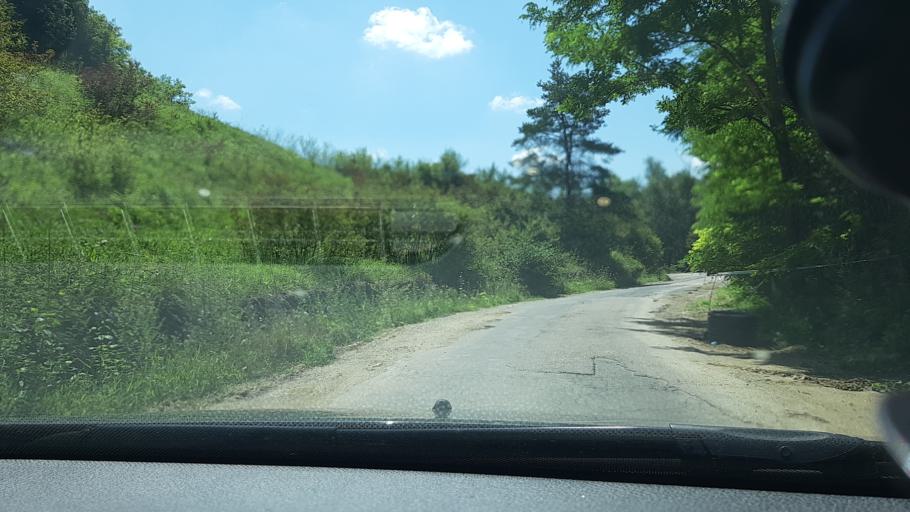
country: RO
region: Hunedoara
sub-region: Comuna Teliucu Inferior
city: Teliucu Inferior
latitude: 45.6849
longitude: 22.8730
